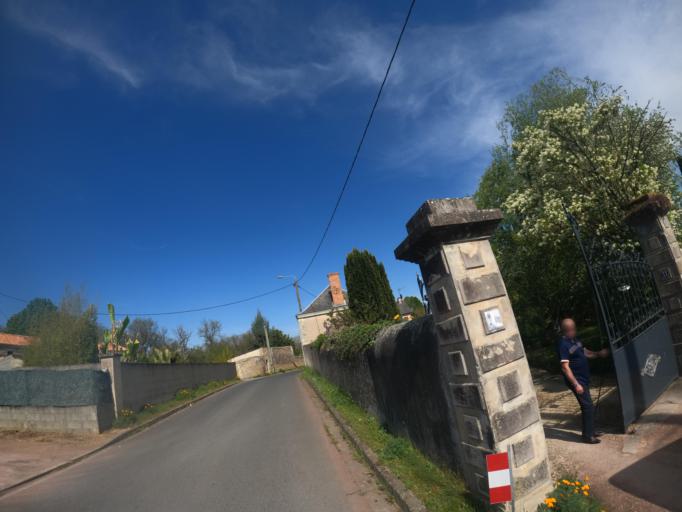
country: FR
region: Poitou-Charentes
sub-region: Departement des Deux-Sevres
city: Saint-Varent
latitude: 46.9159
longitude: -0.2128
